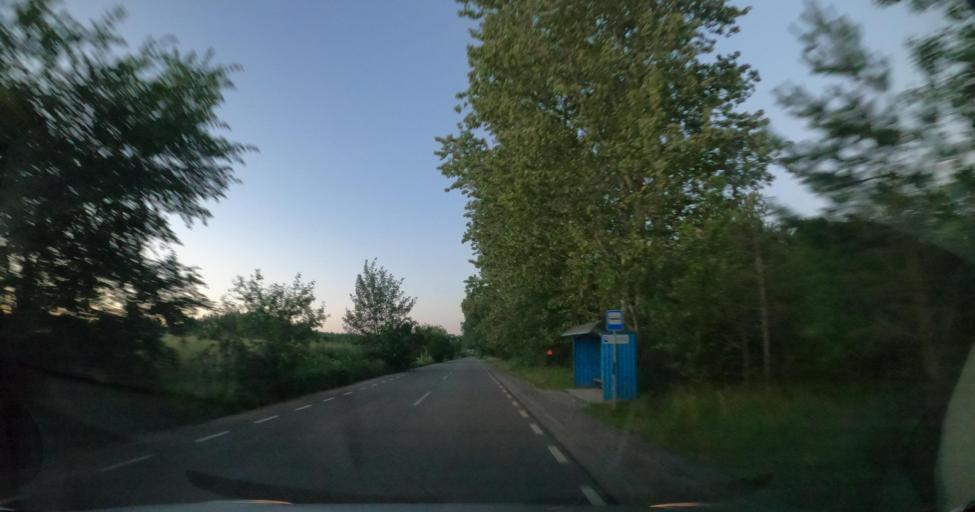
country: PL
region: Pomeranian Voivodeship
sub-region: Powiat wejherowski
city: Szemud
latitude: 54.4746
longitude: 18.1763
